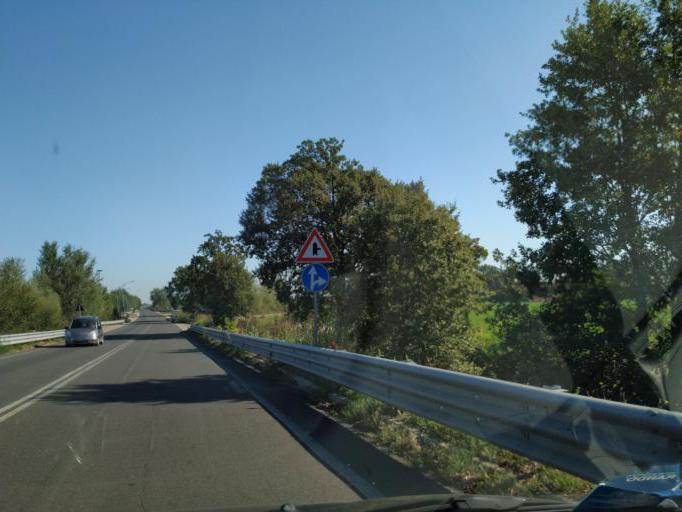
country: IT
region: Emilia-Romagna
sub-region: Provincia di Bologna
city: San Giovanni in Persiceto
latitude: 44.6597
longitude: 11.1831
